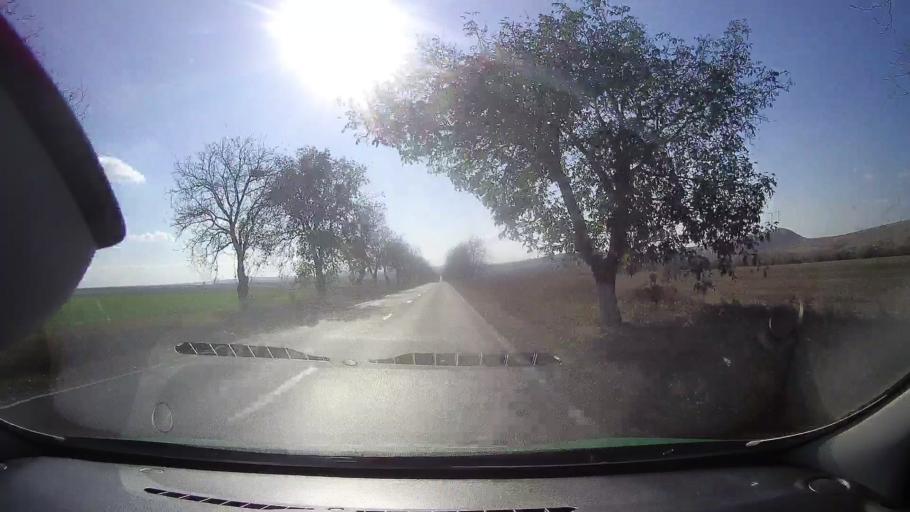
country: RO
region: Tulcea
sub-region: Comuna Ceamurlia de Jos
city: Ceamurlia de Jos
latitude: 44.7842
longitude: 28.6894
